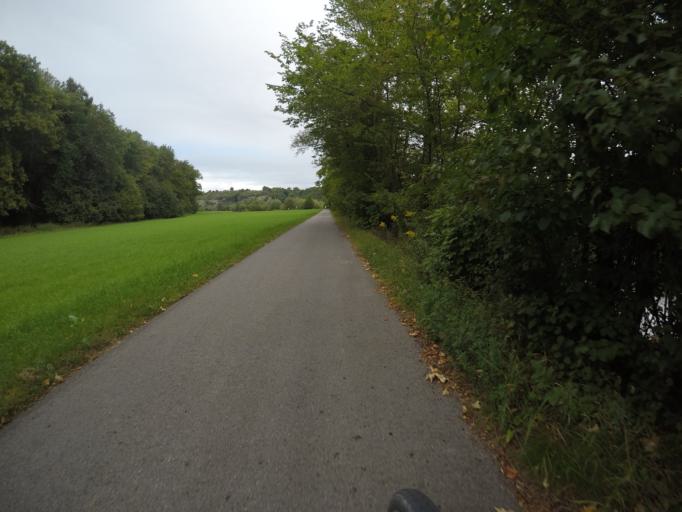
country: DE
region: Baden-Wuerttemberg
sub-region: Regierungsbezirk Stuttgart
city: Marbach am Neckar
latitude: 48.9034
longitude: 9.2570
